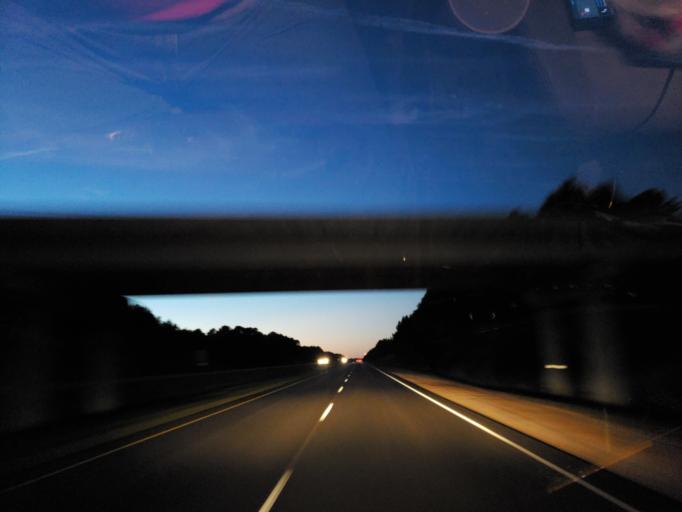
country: US
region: Mississippi
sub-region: Clarke County
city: Quitman
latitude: 32.0768
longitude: -88.6896
